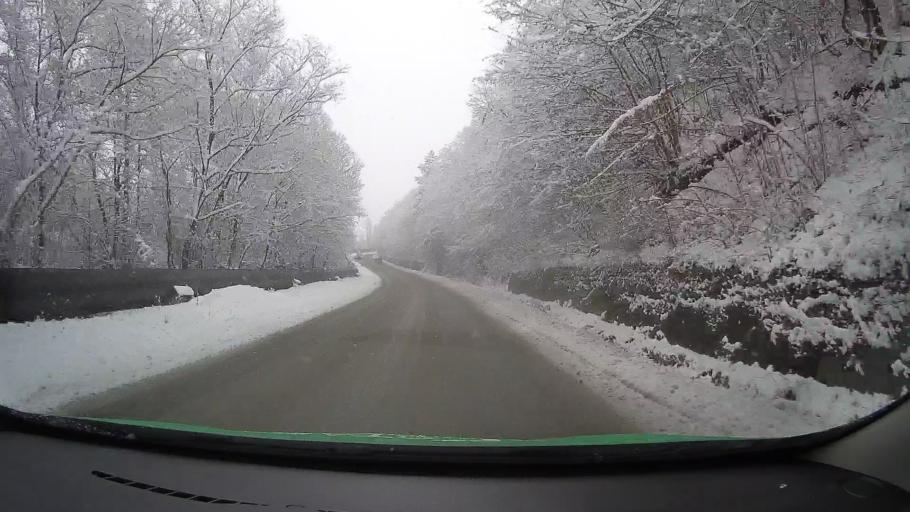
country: RO
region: Hunedoara
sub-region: Comuna Teliucu Inferior
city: Teliucu Inferior
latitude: 45.7236
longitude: 22.8798
